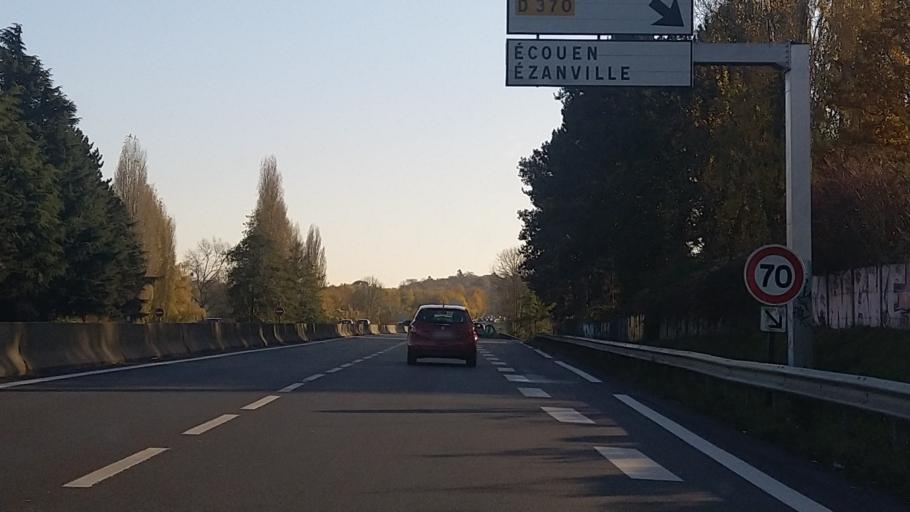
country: FR
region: Ile-de-France
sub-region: Departement du Val-d'Oise
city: Moisselles
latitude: 49.0368
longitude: 2.3451
